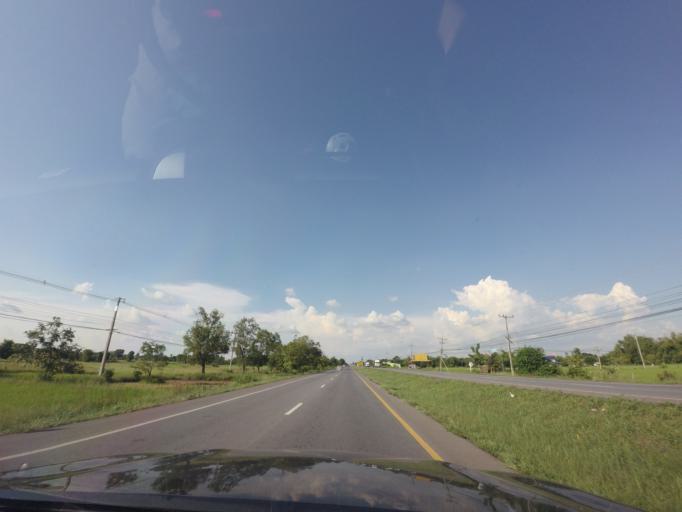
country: TH
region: Khon Kaen
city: Non Sila
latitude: 15.9873
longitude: 102.6977
